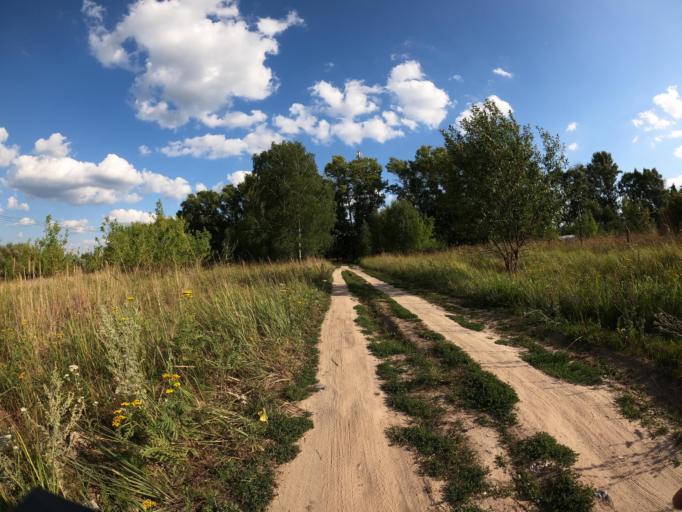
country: RU
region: Moskovskaya
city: Peski
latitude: 55.1931
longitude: 38.7468
